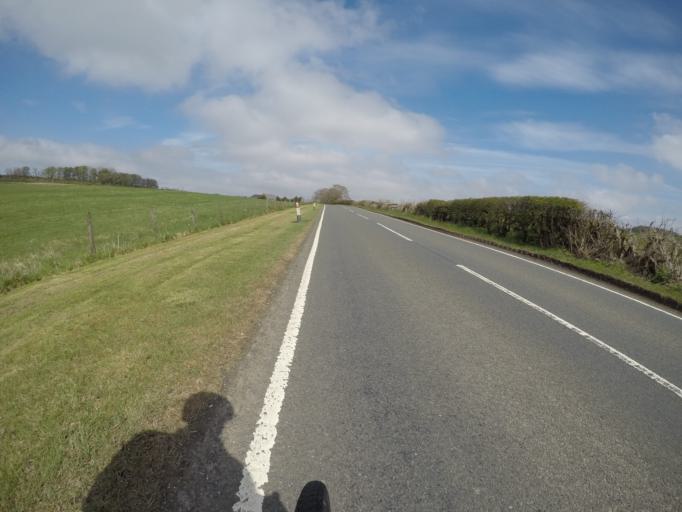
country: GB
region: Scotland
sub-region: East Ayrshire
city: Stewarton
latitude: 55.7082
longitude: -4.4594
